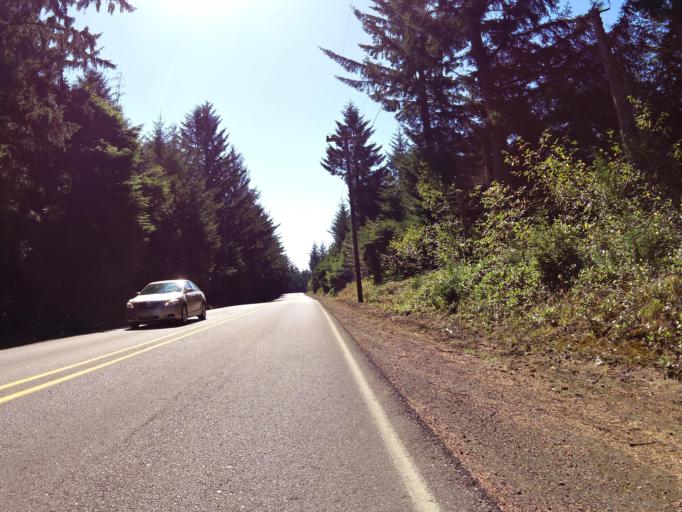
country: US
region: Oregon
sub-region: Coos County
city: Barview
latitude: 43.3224
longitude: -124.3419
